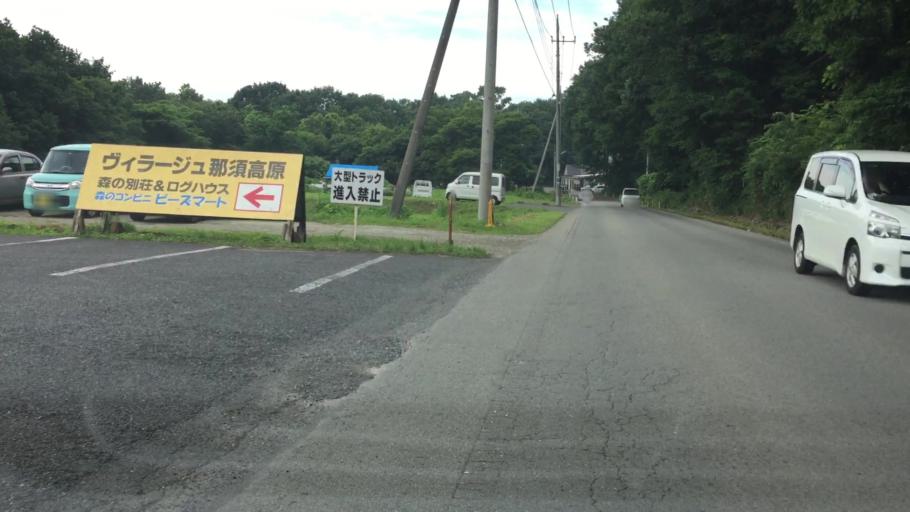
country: JP
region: Tochigi
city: Kuroiso
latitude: 37.0705
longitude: 140.0445
